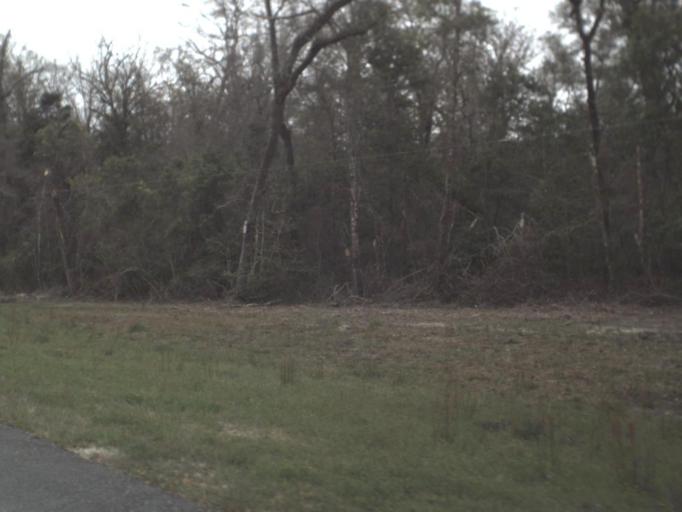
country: US
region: Florida
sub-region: Wakulla County
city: Crawfordville
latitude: 30.1174
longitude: -84.3719
